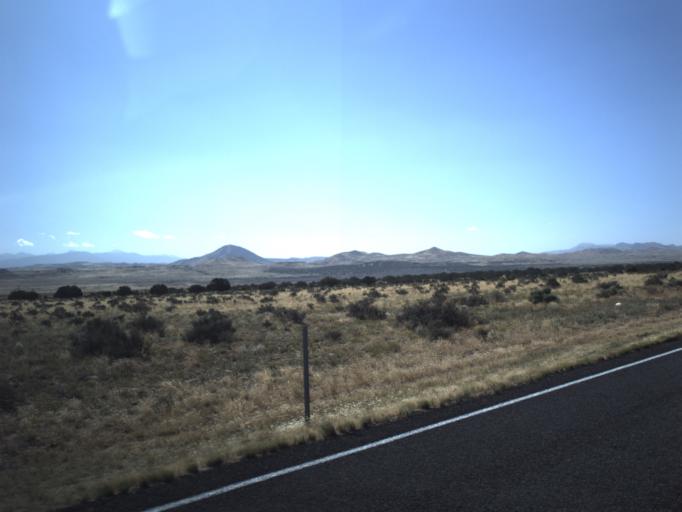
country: US
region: Utah
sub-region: Beaver County
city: Milford
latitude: 38.8450
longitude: -112.8442
